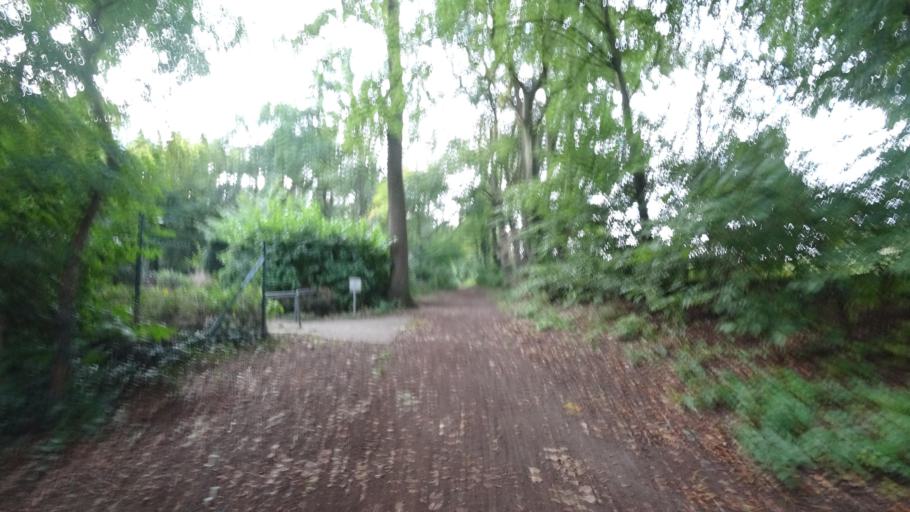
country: DE
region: North Rhine-Westphalia
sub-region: Regierungsbezirk Detmold
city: Guetersloh
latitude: 51.9064
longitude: 8.3376
